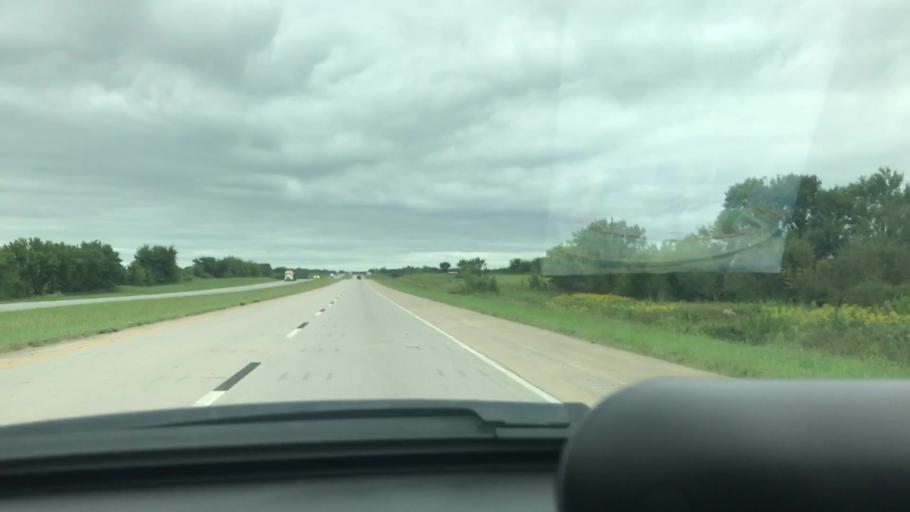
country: US
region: Oklahoma
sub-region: Mayes County
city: Chouteau
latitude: 36.0780
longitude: -95.3644
